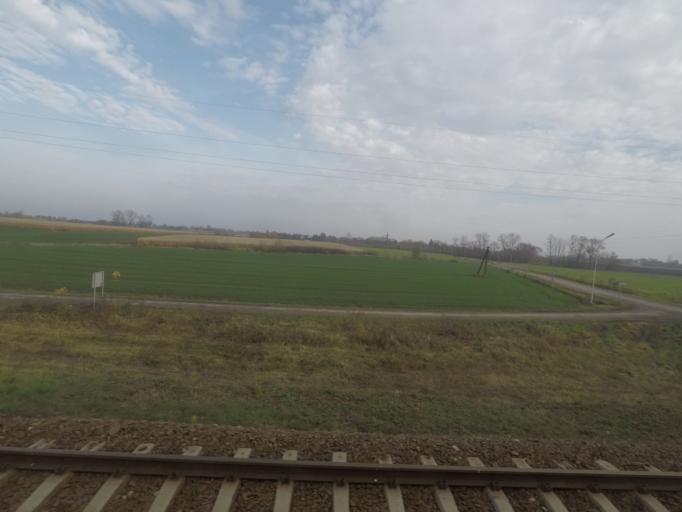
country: PL
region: Subcarpathian Voivodeship
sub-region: Powiat jaroslawski
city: Sosnica
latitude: 49.8985
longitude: 22.8529
